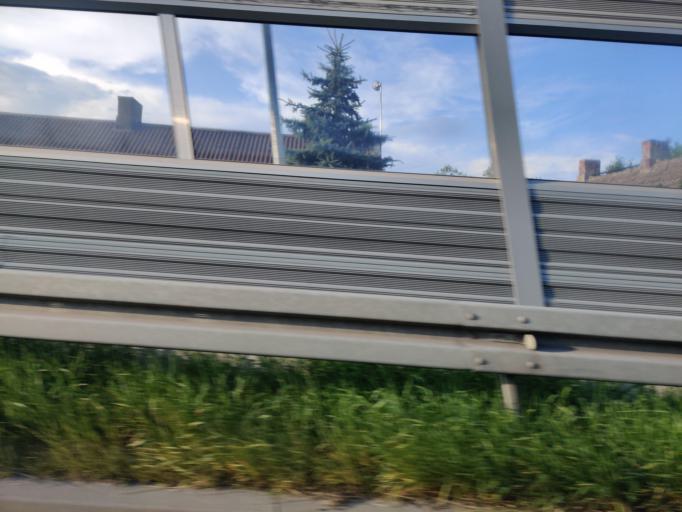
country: PL
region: Greater Poland Voivodeship
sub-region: Konin
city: Konin
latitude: 52.2028
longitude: 18.2741
